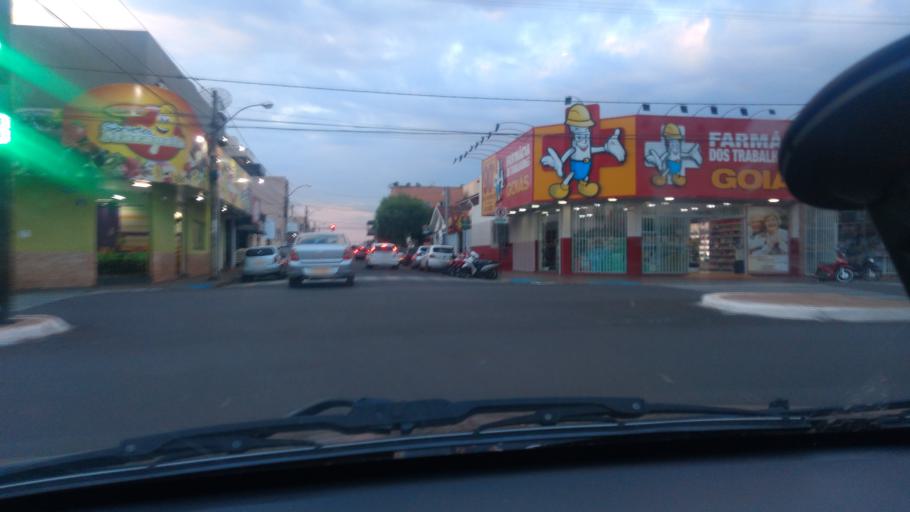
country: BR
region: Goias
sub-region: Santa Helena De Goias
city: Santa Helena de Goias
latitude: -17.7947
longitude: -50.9308
